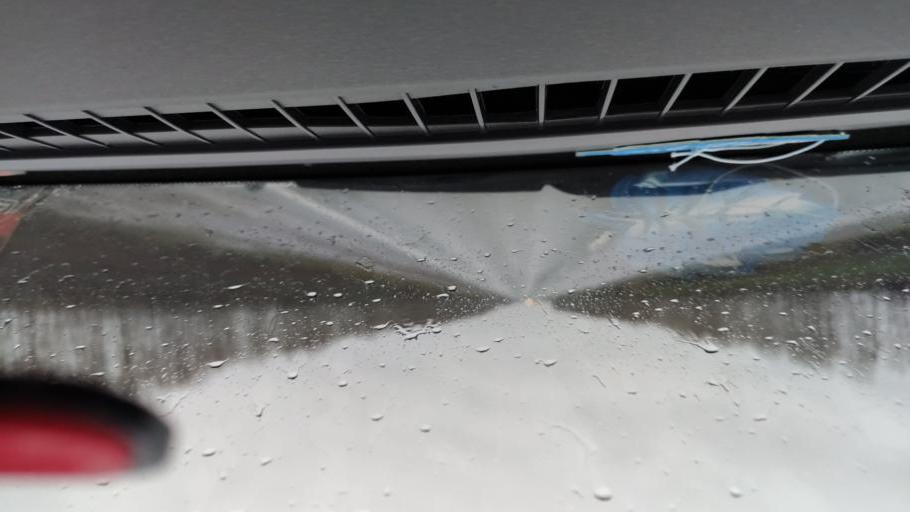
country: RU
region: Tatarstan
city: Mendeleyevsk
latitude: 55.9323
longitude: 52.2833
